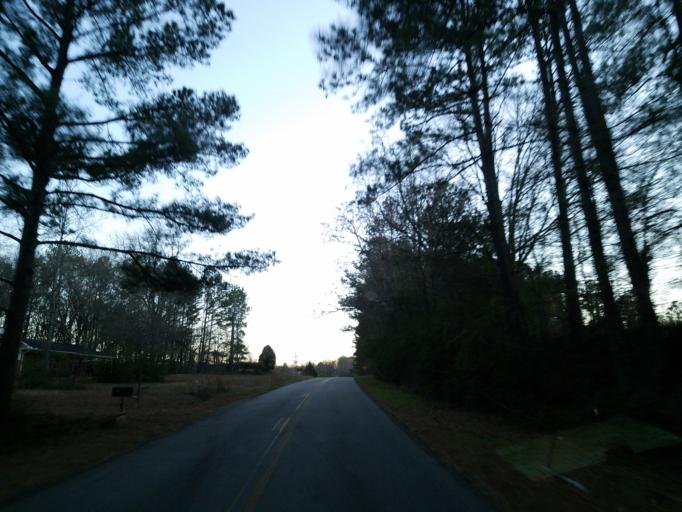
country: US
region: Georgia
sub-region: Monroe County
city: Forsyth
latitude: 32.9902
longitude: -83.8792
